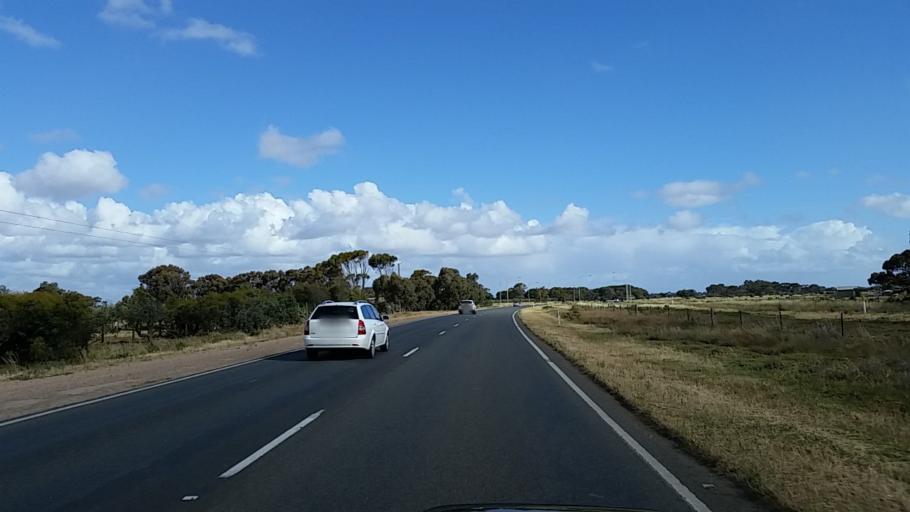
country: AU
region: South Australia
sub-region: Mallala
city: Two Wells
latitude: -34.6005
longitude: 138.5147
